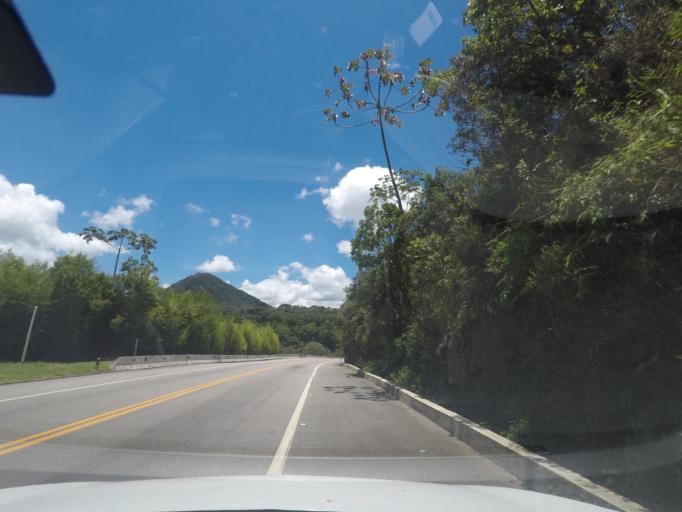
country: BR
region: Rio de Janeiro
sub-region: Teresopolis
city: Teresopolis
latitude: -22.4587
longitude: -42.9771
